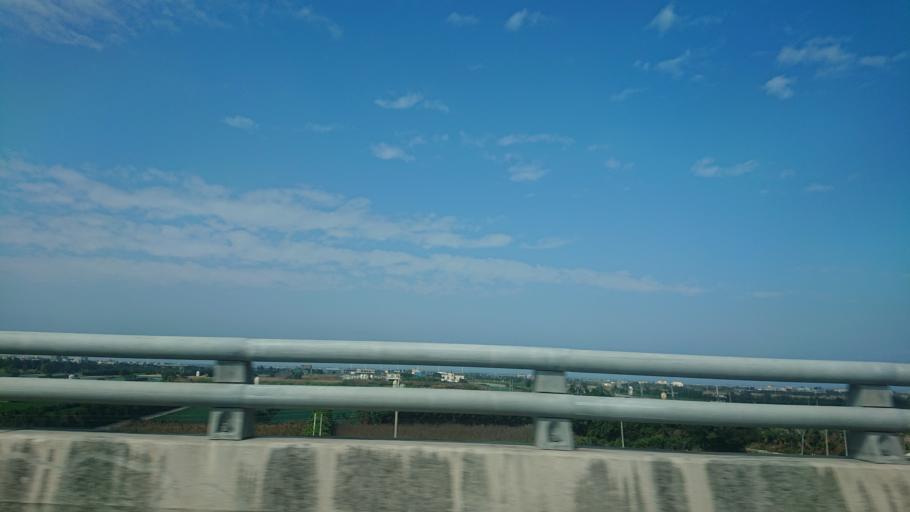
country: TW
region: Taiwan
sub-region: Changhua
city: Chang-hua
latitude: 23.9785
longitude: 120.3631
